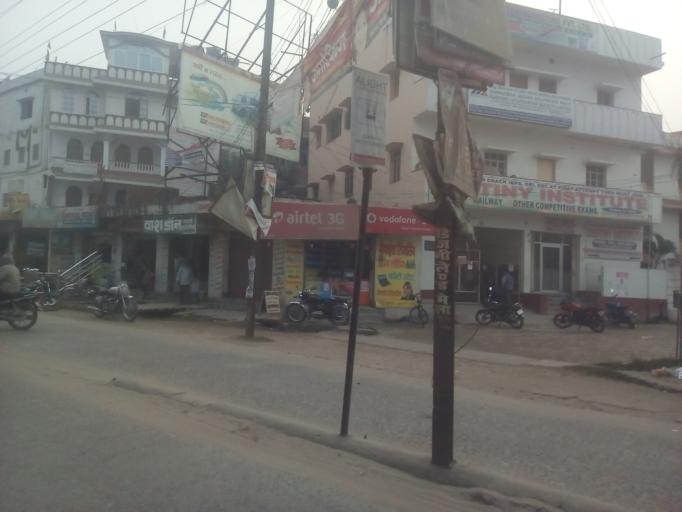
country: IN
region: Bihar
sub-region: Muzaffarpur
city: Muzaffarpur
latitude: 26.1071
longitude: 85.3974
